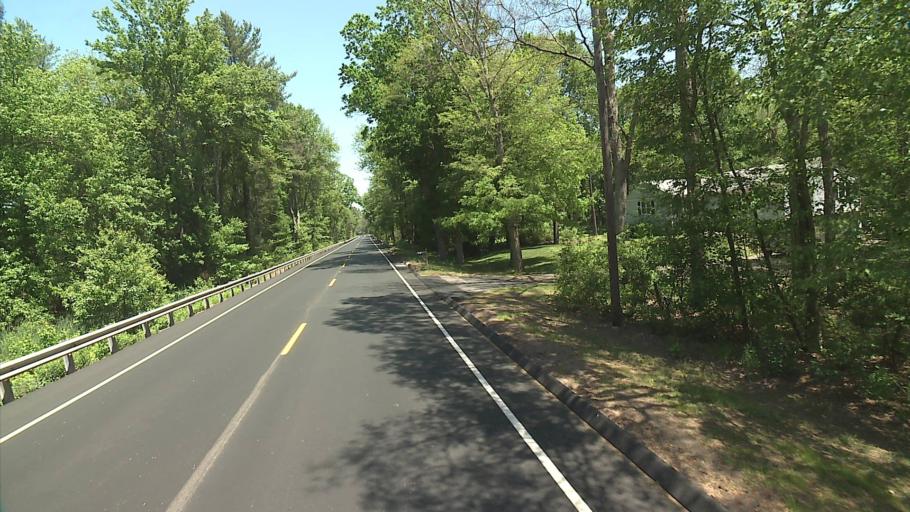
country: US
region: Connecticut
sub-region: Tolland County
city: Crystal Lake
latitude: 41.9558
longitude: -72.3685
